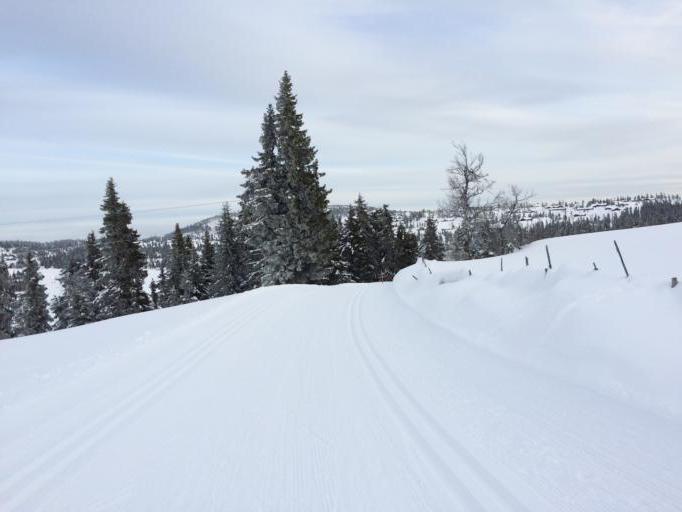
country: NO
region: Oppland
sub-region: Gausdal
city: Segalstad bru
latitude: 61.3124
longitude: 10.0556
